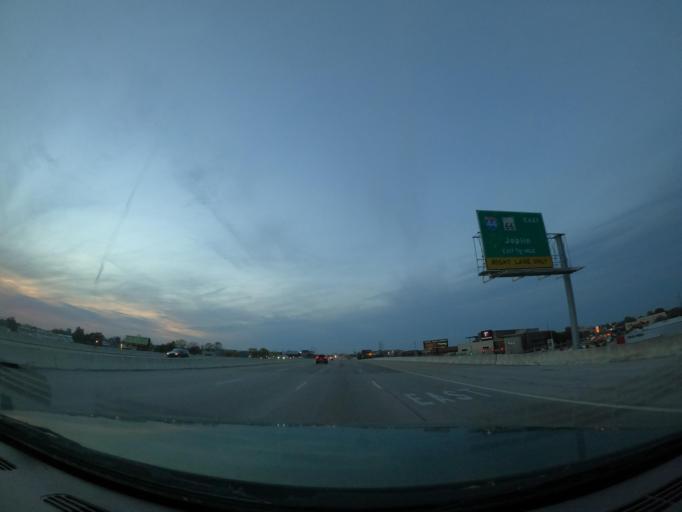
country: US
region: Oklahoma
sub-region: Tulsa County
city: Broken Arrow
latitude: 36.1082
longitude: -95.8858
